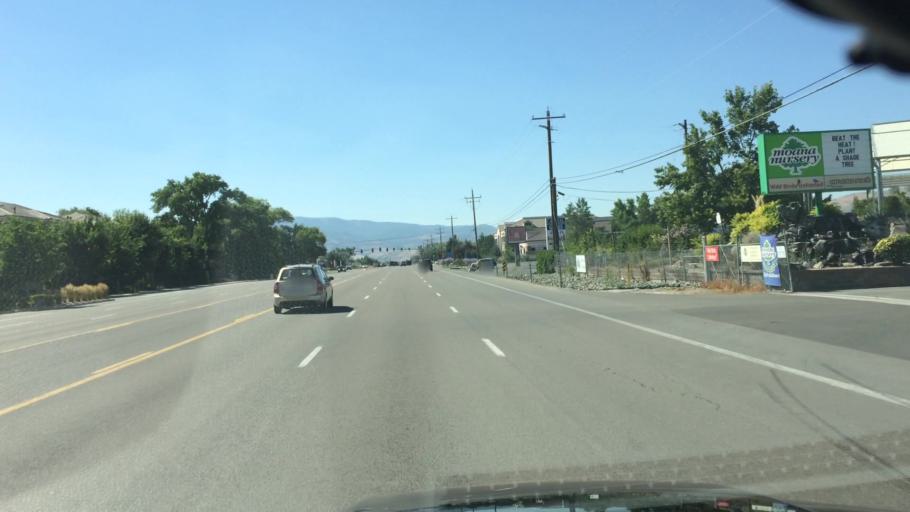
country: US
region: Nevada
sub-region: Washoe County
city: Sparks
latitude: 39.4294
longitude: -119.7635
